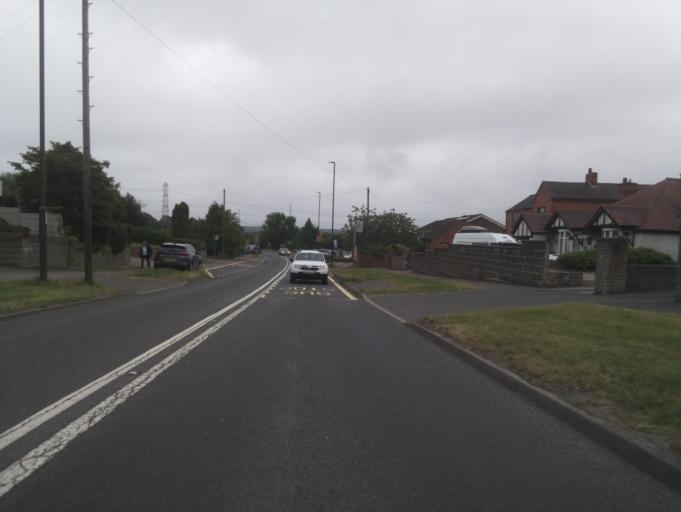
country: GB
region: England
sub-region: Staffordshire
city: Burton upon Trent
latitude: 52.7788
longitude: -1.6066
